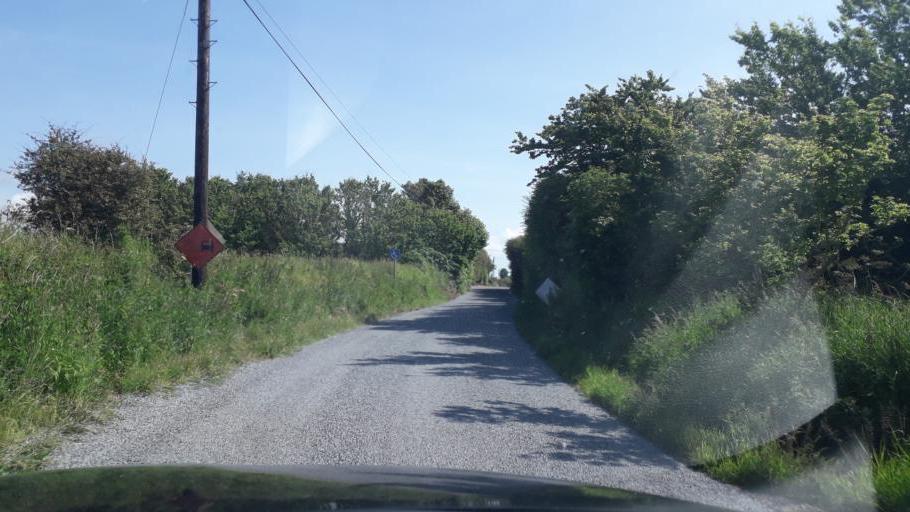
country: IE
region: Leinster
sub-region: Loch Garman
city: Loch Garman
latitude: 52.1925
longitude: -6.5497
